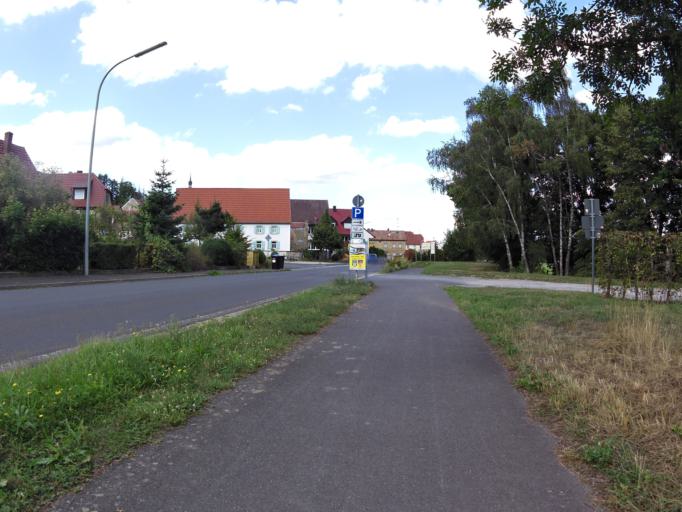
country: DE
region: Bavaria
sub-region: Regierungsbezirk Unterfranken
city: Grafenrheinfeld
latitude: 49.9718
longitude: 10.1730
